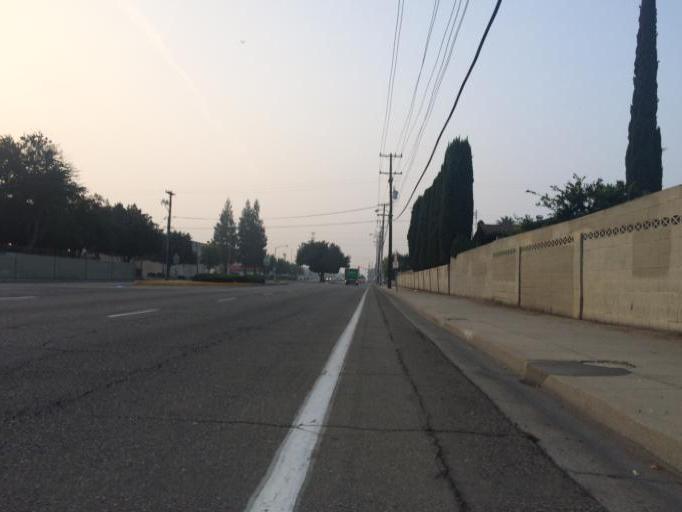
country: US
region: California
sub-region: Fresno County
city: Fresno
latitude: 36.7674
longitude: -119.7364
